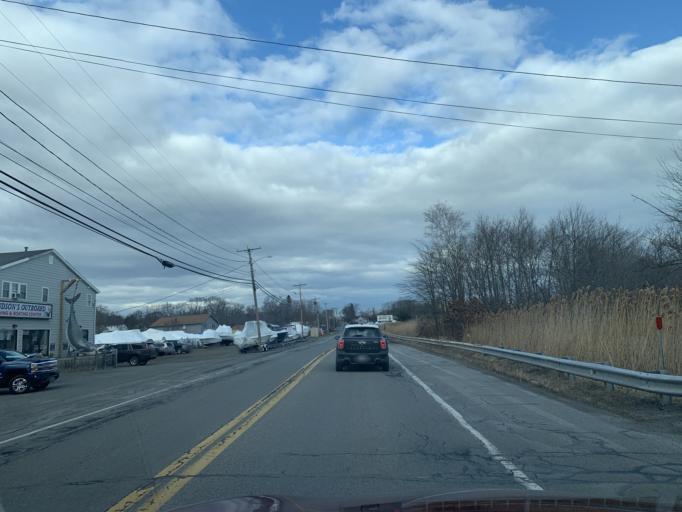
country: US
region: Massachusetts
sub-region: Essex County
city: Salisbury
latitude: 42.8345
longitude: -70.8619
